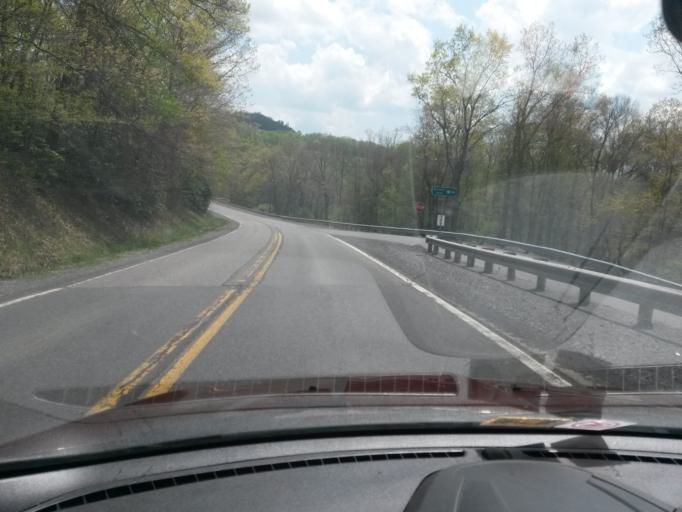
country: US
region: West Virginia
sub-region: Greenbrier County
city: Rainelle
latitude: 38.0373
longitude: -80.7304
